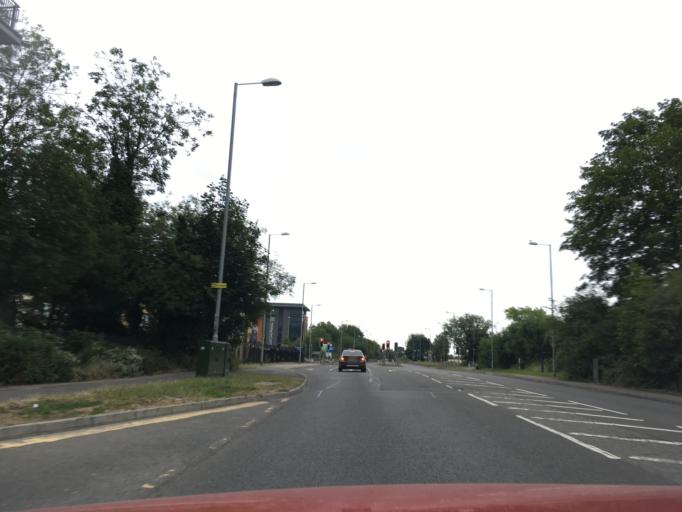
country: GB
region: England
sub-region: Central Bedfordshire
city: Kensworth
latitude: 51.8742
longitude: -0.5029
